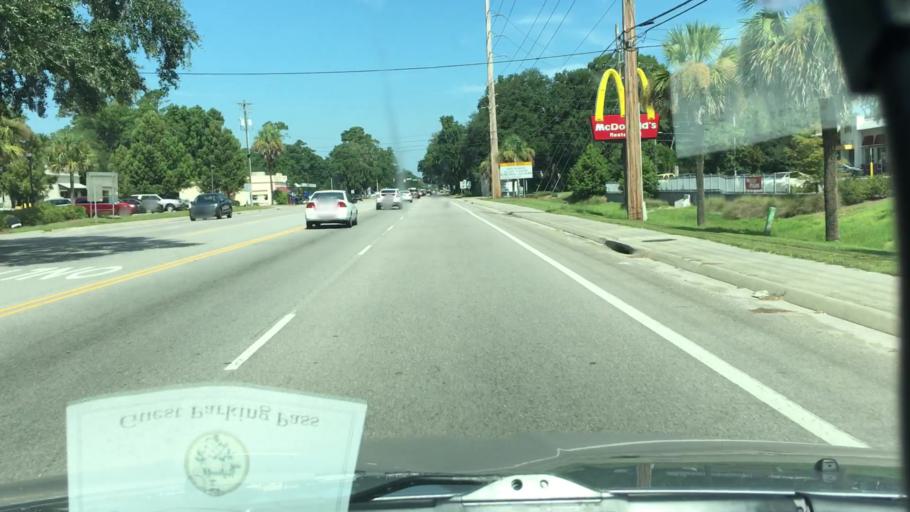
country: US
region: South Carolina
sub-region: Beaufort County
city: Beaufort
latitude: 32.4123
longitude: -80.6471
